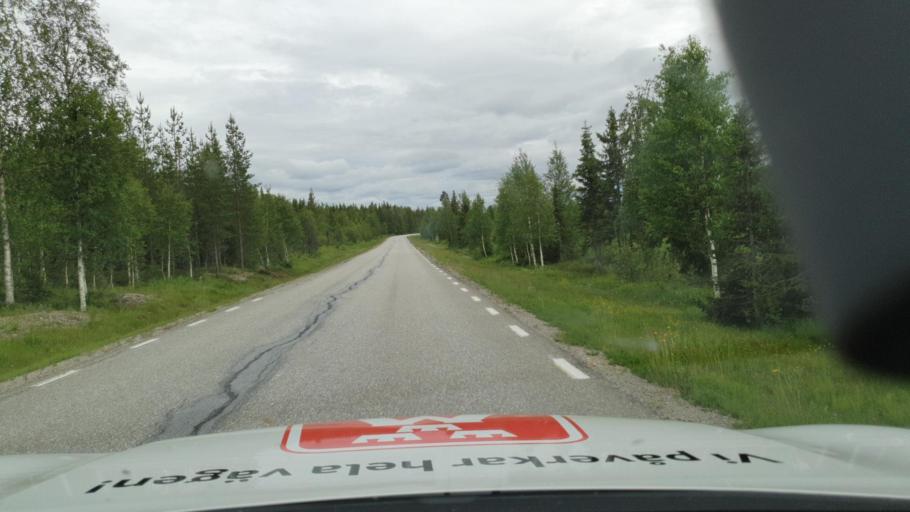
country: SE
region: Vaesterbotten
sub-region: Lycksele Kommun
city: Soderfors
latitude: 64.3244
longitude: 18.1523
